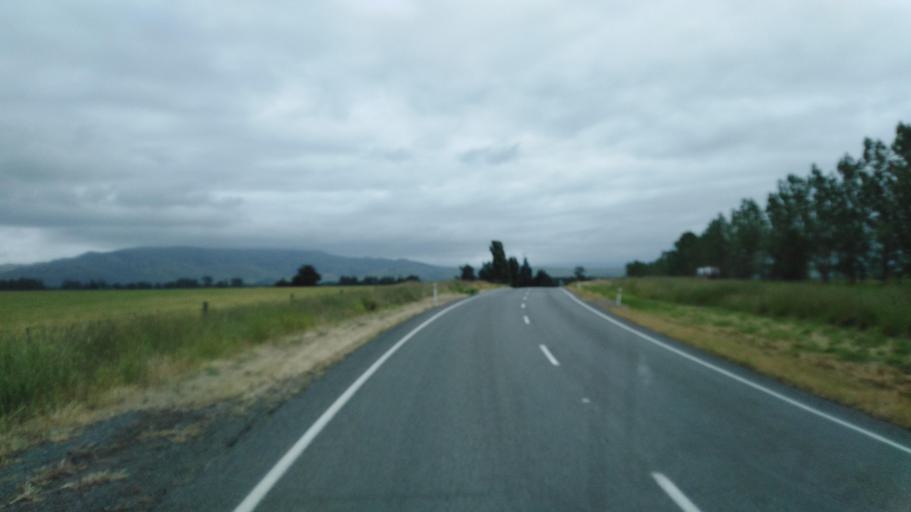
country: NZ
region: Canterbury
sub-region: Kaikoura District
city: Kaikoura
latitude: -42.7498
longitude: 173.2684
